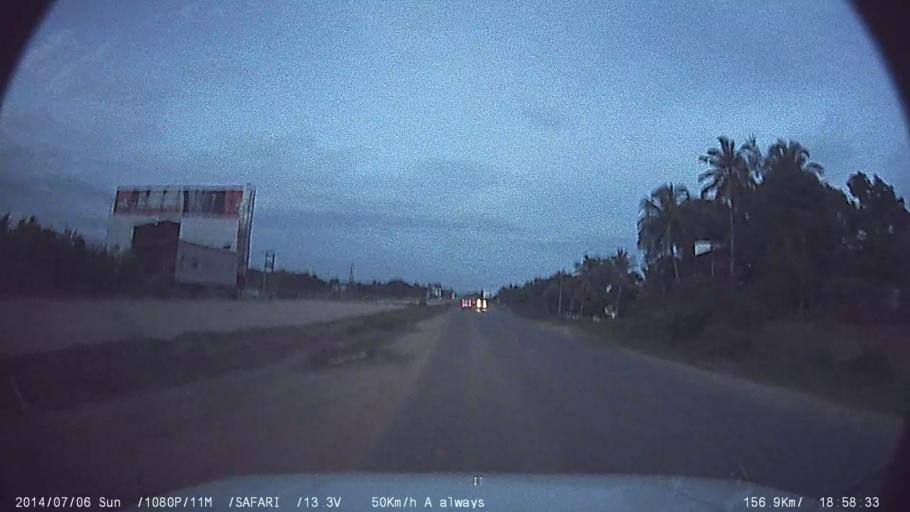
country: IN
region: Kerala
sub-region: Palakkad district
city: Palakkad
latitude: 10.7391
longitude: 76.6415
